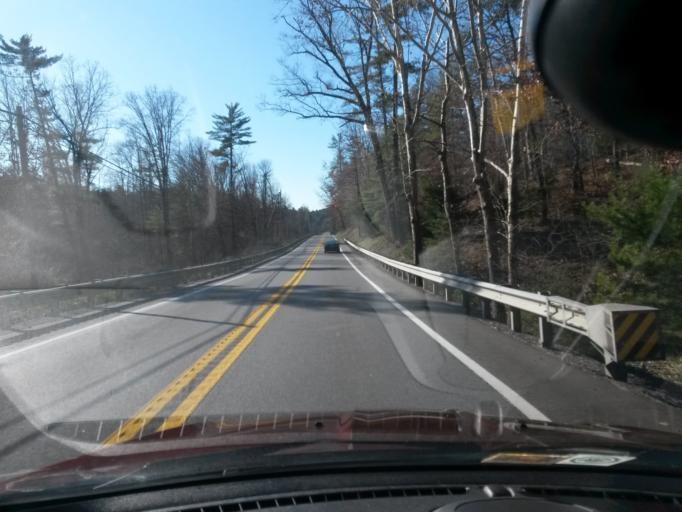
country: US
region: Virginia
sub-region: Alleghany County
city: Clifton Forge
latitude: 37.7119
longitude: -79.8118
